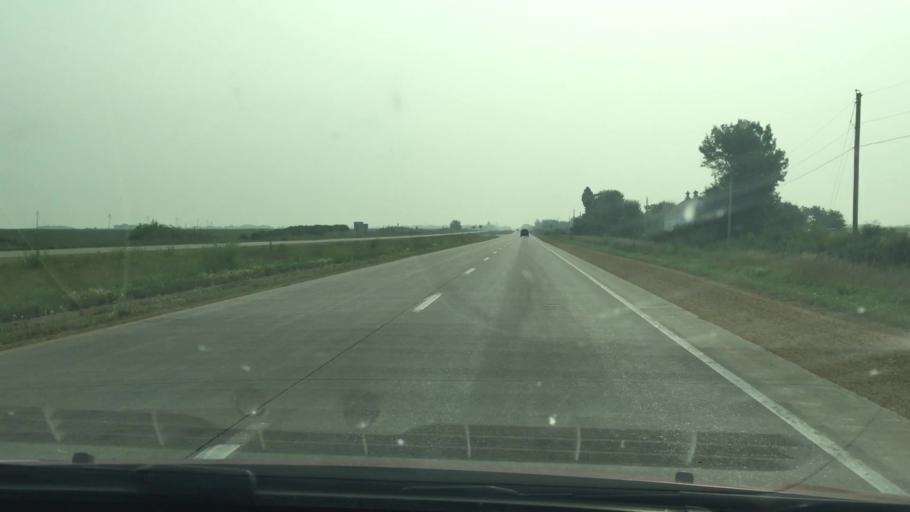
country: US
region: Iowa
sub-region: Scott County
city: Blue Grass
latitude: 41.5089
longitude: -90.7309
